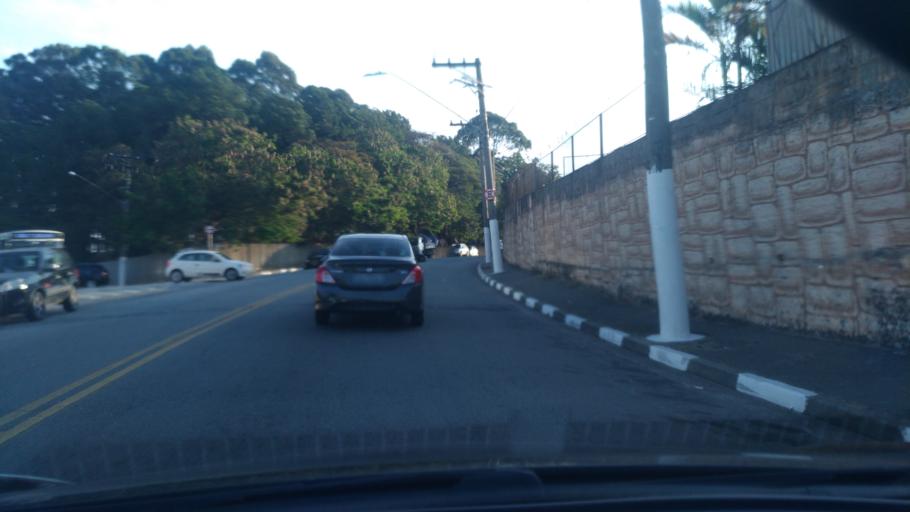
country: BR
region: Sao Paulo
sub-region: Osasco
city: Osasco
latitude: -23.5358
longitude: -46.7924
